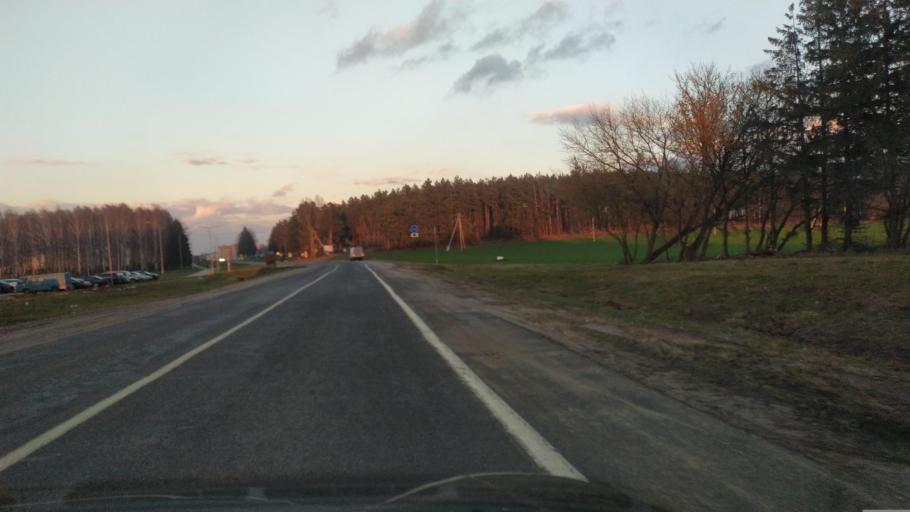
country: BY
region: Brest
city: Kamyanyets
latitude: 52.3876
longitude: 23.8177
